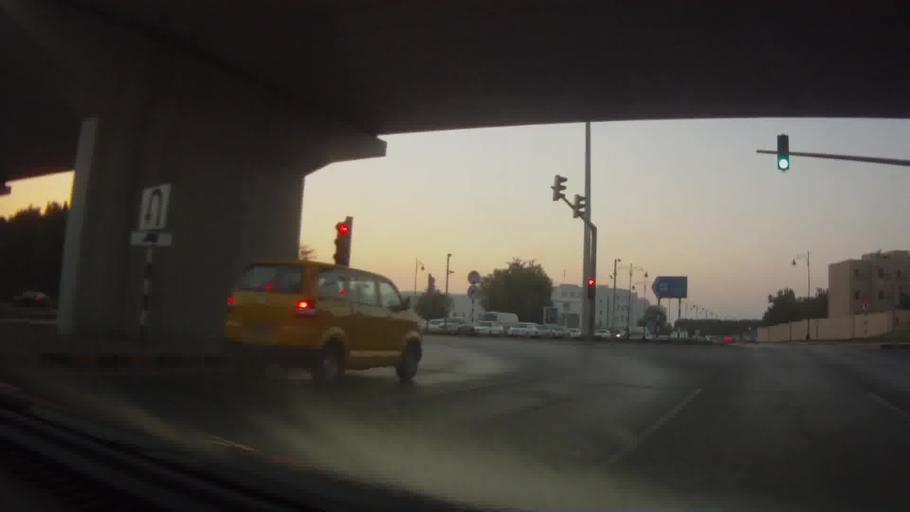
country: OM
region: Muhafazat Masqat
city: Bawshar
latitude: 23.5984
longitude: 58.4435
